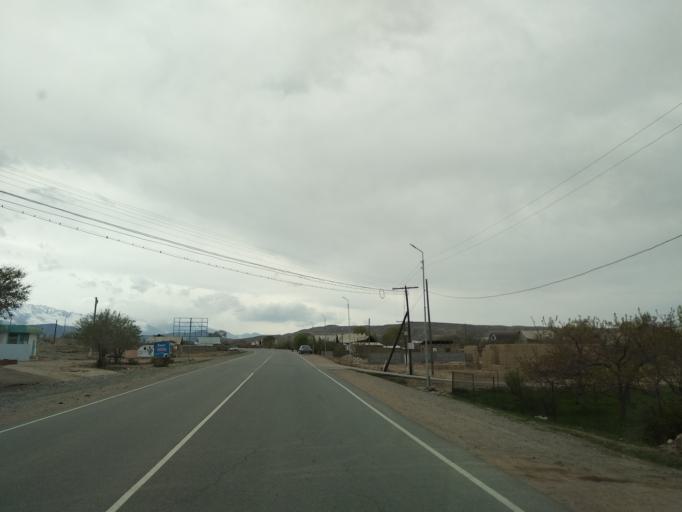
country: KG
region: Ysyk-Koel
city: Bokombayevskoye
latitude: 42.1524
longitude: 77.0395
